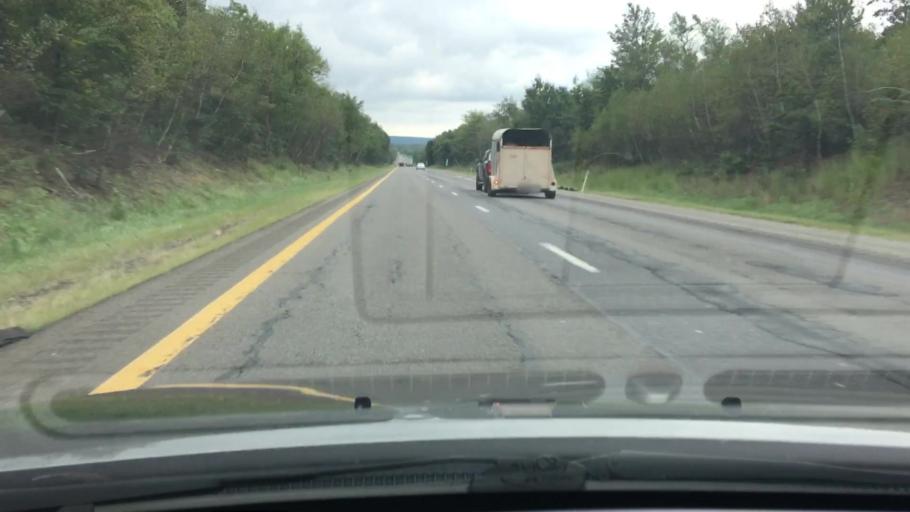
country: US
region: Pennsylvania
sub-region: Schuylkill County
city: Girardville
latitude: 40.7667
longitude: -76.2660
